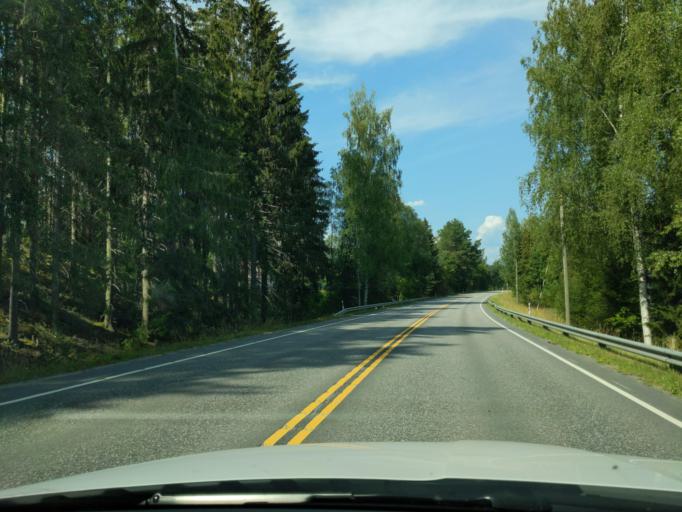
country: FI
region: Paijanne Tavastia
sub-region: Lahti
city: Padasjoki
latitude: 61.3827
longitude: 25.1910
